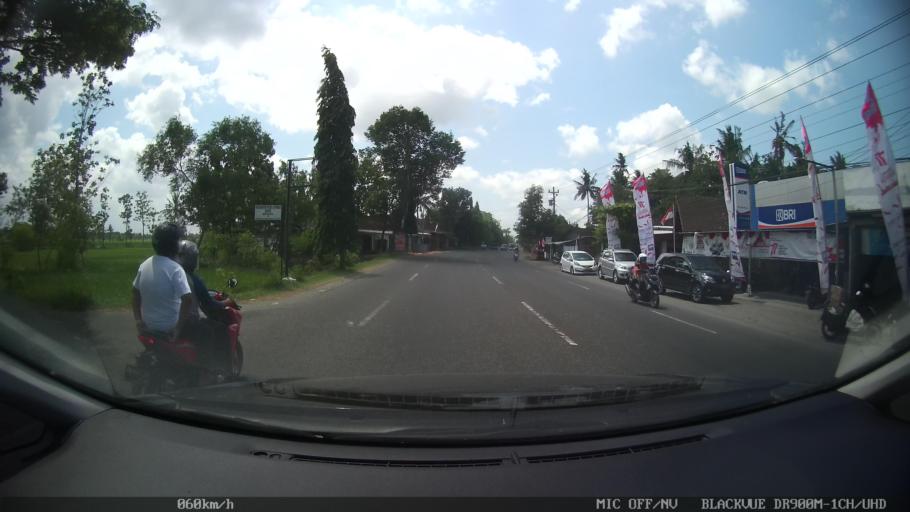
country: ID
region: Daerah Istimewa Yogyakarta
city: Pandak
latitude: -7.9079
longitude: 110.3025
